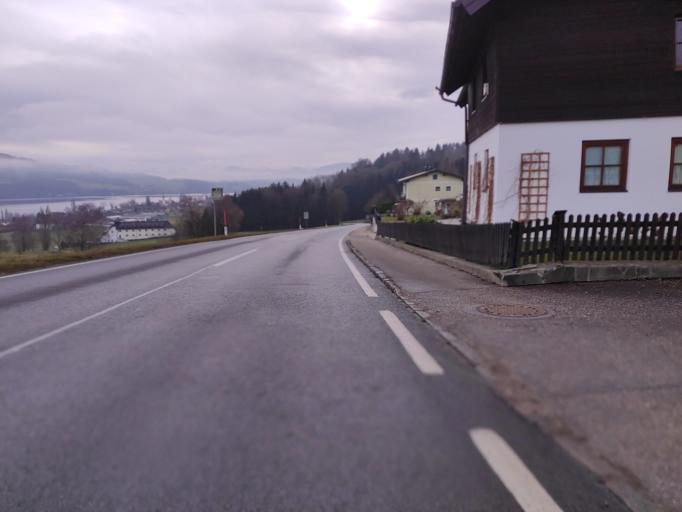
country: AT
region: Salzburg
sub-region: Politischer Bezirk Salzburg-Umgebung
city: Berndorf bei Salzburg
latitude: 47.9779
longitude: 13.0715
